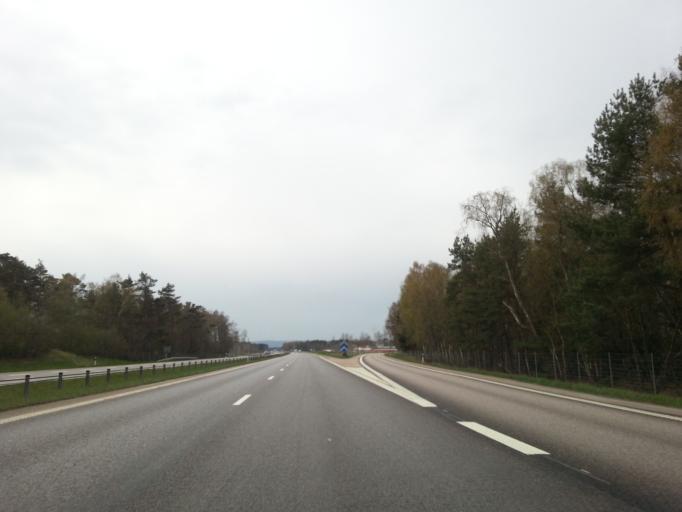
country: SE
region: Halland
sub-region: Laholms Kommun
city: Mellbystrand
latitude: 56.5095
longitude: 12.9620
